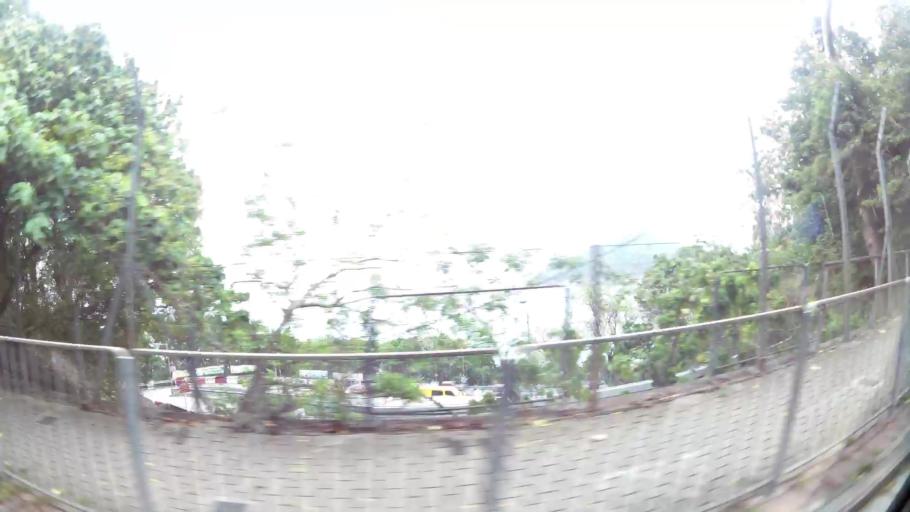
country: HK
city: Hong Kong
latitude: 22.2779
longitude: 114.1175
